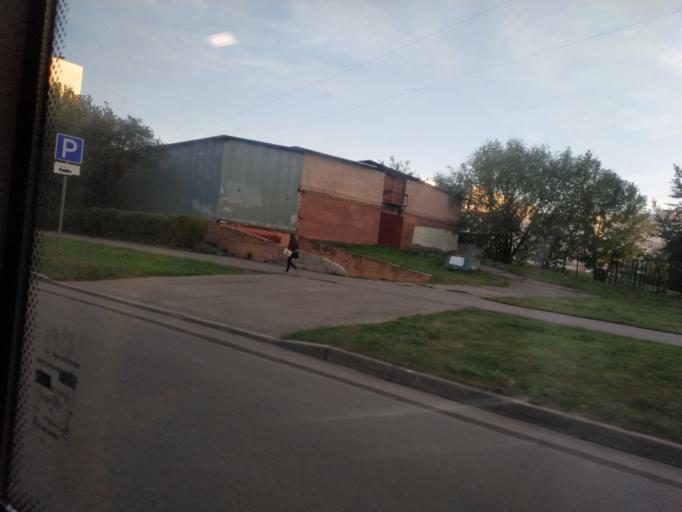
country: RU
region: Moscow
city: Novo-Peredelkino
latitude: 55.6465
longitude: 37.3464
